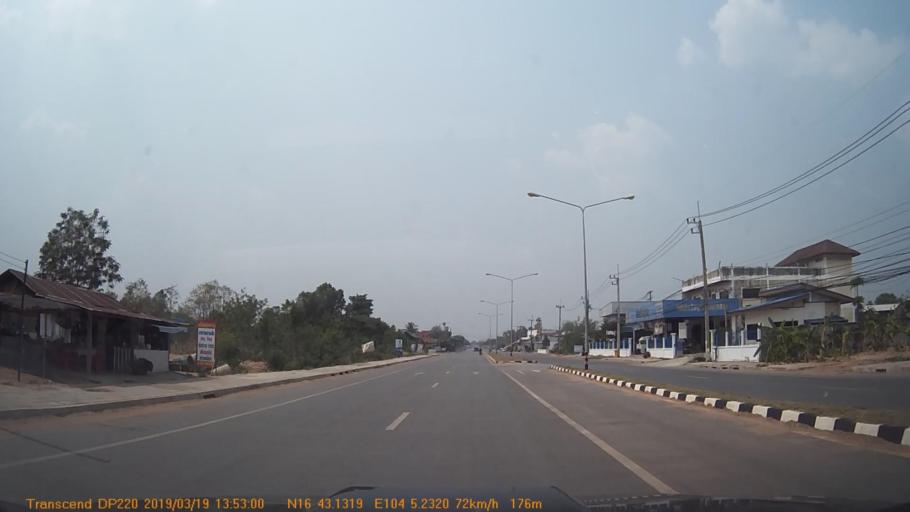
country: TH
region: Kalasin
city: Khao Wong
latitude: 16.7194
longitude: 104.0870
